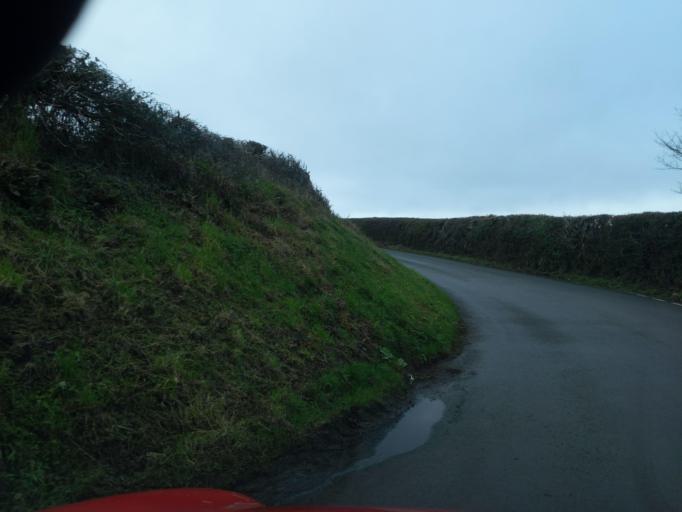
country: GB
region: England
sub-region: Devon
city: Wembury
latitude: 50.3286
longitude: -4.0913
